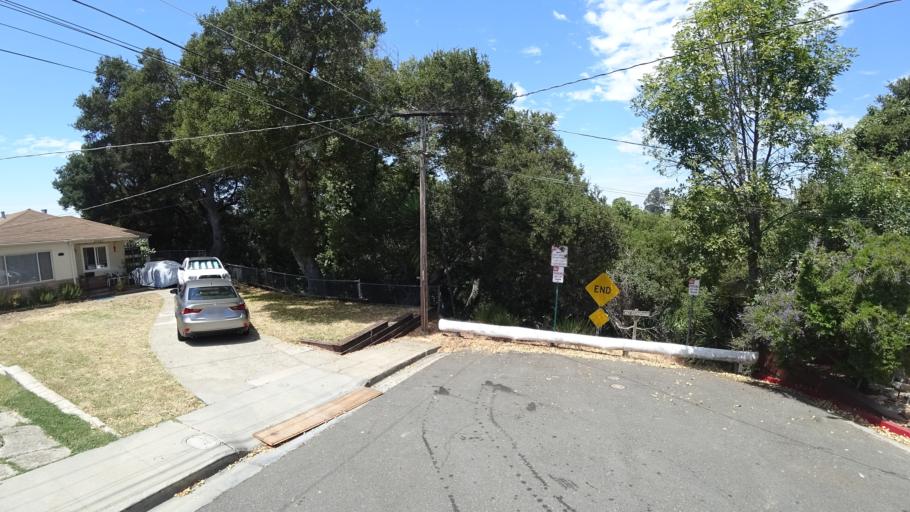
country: US
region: California
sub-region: Alameda County
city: Hayward
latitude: 37.6661
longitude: -122.0743
